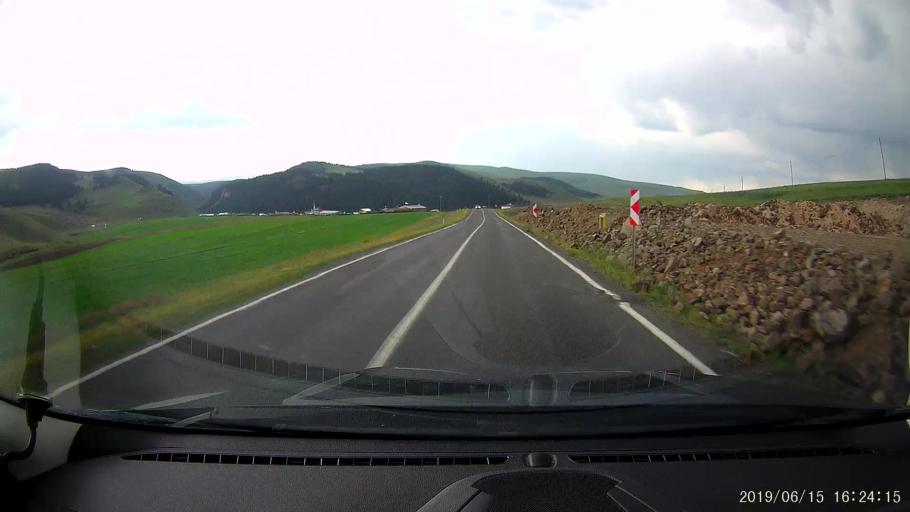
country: TR
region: Ardahan
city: Hanak
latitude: 41.1669
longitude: 42.8692
